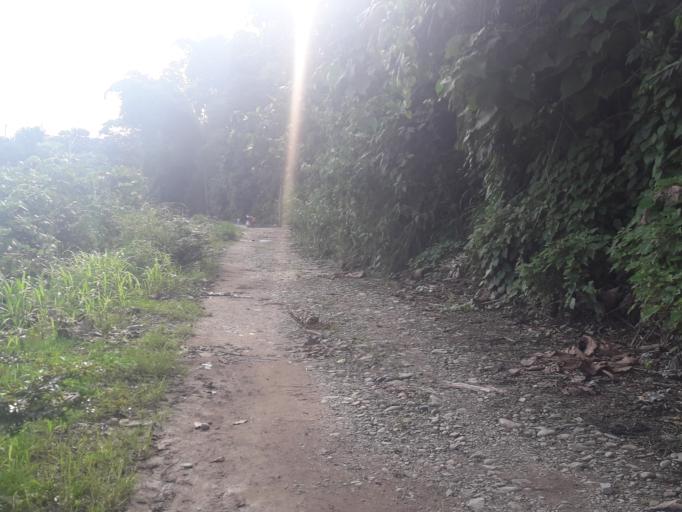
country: EC
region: Napo
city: Tena
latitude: -0.9893
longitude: -77.8125
